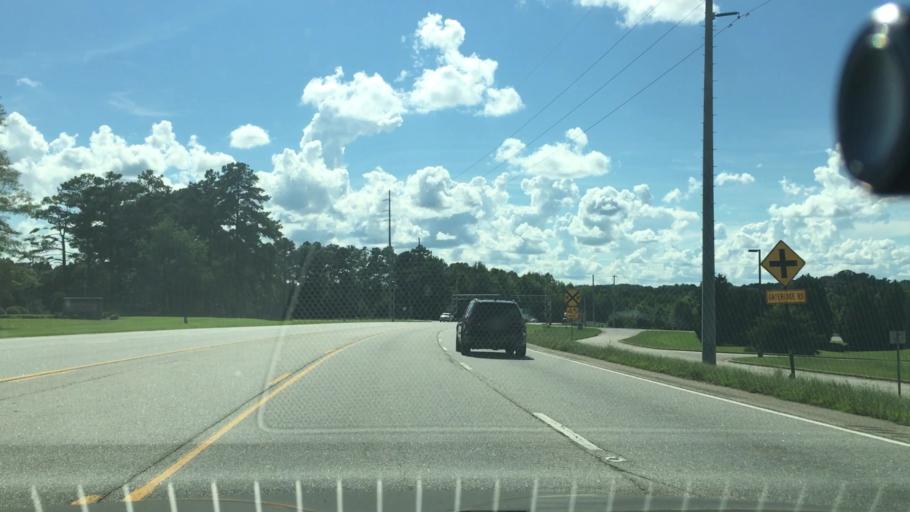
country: US
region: Georgia
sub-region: Spalding County
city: East Griffin
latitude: 33.2325
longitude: -84.2350
